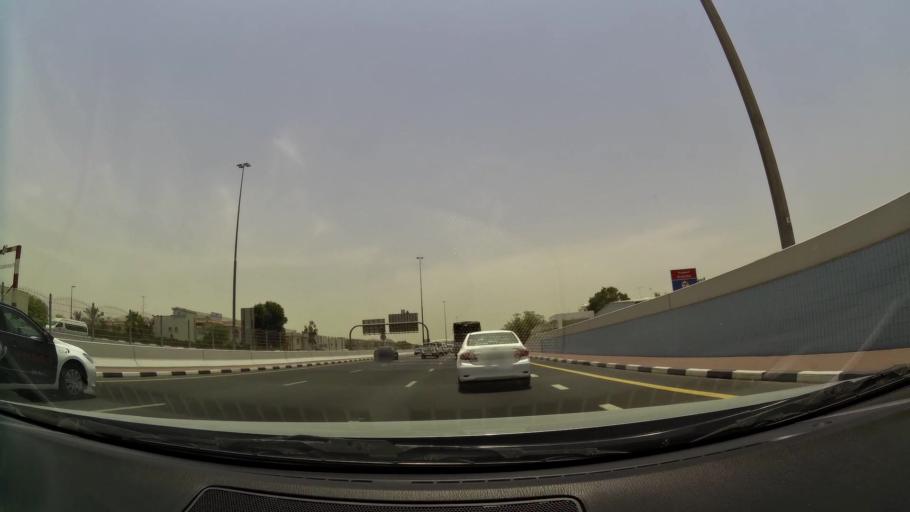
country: AE
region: Ash Shariqah
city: Sharjah
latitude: 25.2343
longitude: 55.3777
